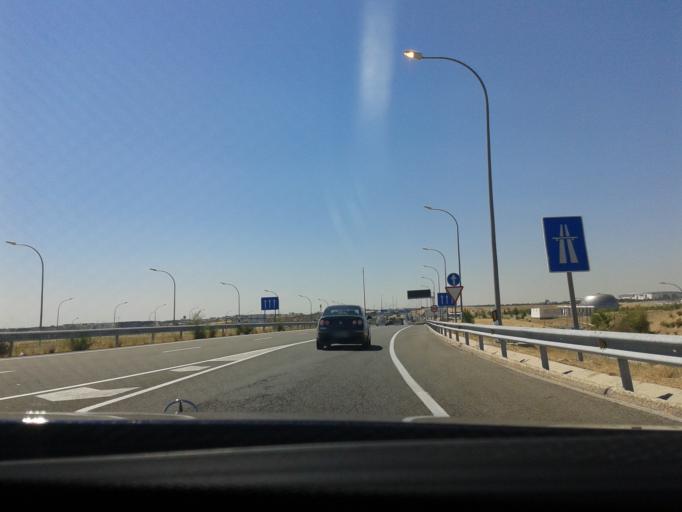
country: ES
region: Madrid
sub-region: Provincia de Madrid
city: Barajas de Madrid
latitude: 40.4921
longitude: -3.6025
